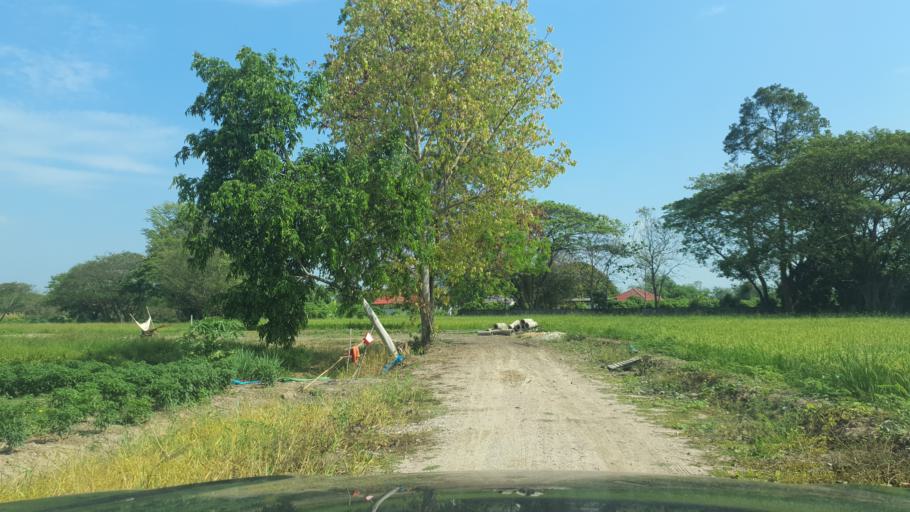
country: TH
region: Chiang Mai
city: Saraphi
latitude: 18.7275
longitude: 99.0469
